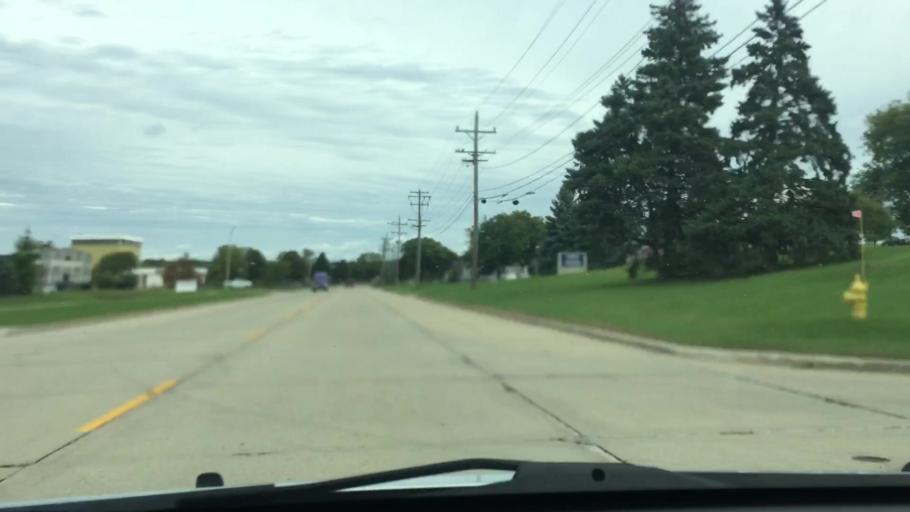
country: US
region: Wisconsin
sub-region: Waukesha County
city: Waukesha
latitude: 42.9914
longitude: -88.2497
